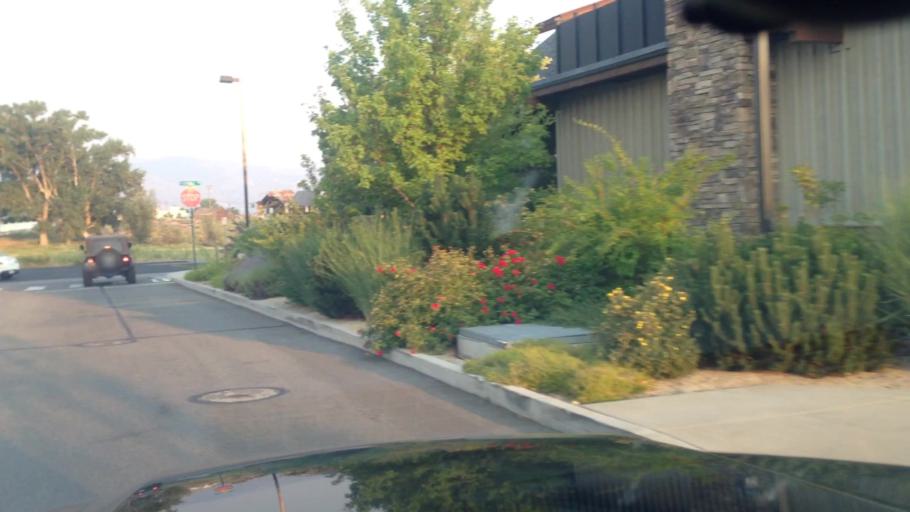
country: US
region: Nevada
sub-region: Washoe County
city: Sparks
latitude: 39.4386
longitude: -119.7715
